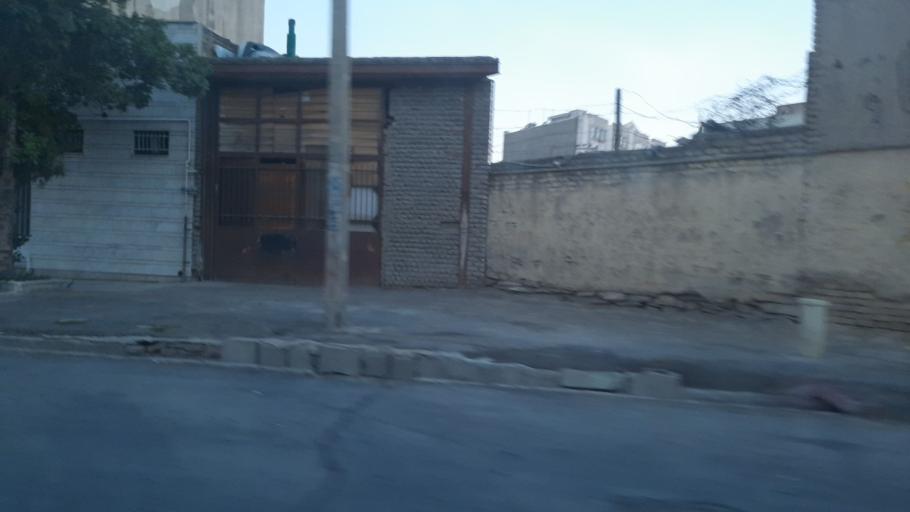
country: IR
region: Markazi
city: Arak
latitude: 34.0768
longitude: 49.6977
